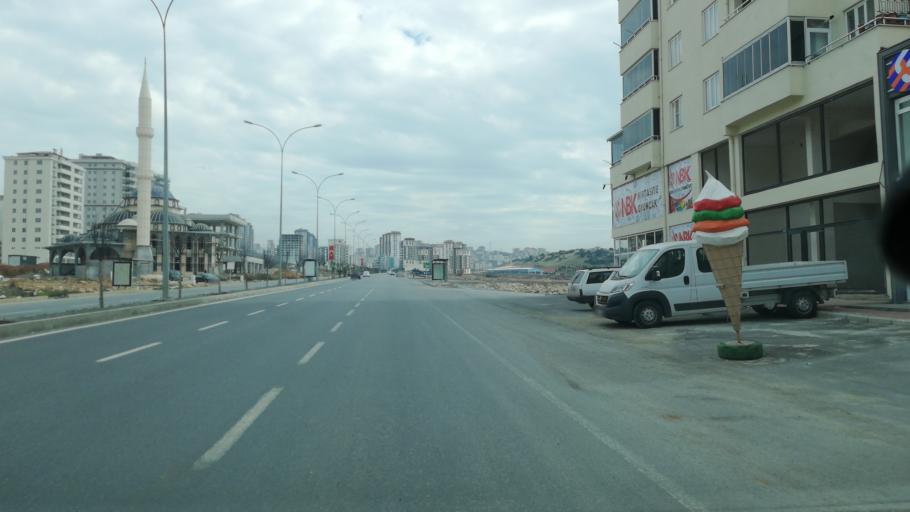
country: TR
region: Kahramanmaras
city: Kahramanmaras
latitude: 37.5894
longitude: 36.8403
